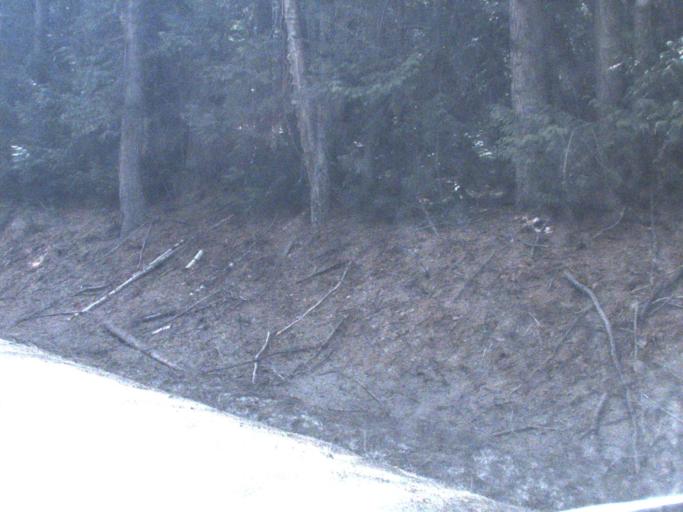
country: US
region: Washington
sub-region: Pend Oreille County
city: Newport
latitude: 48.4479
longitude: -117.3243
